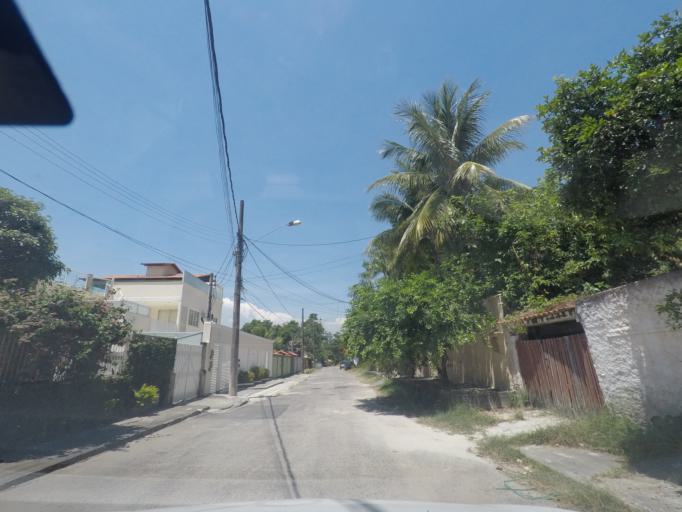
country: BR
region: Rio de Janeiro
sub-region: Niteroi
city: Niteroi
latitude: -22.9689
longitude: -43.0403
